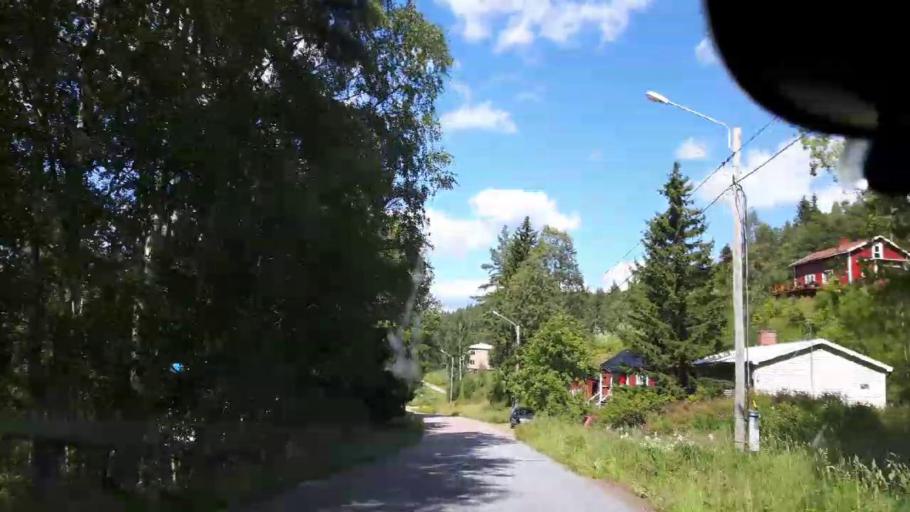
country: SE
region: Jaemtland
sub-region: Ragunda Kommun
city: Hammarstrand
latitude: 62.9524
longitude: 16.6867
